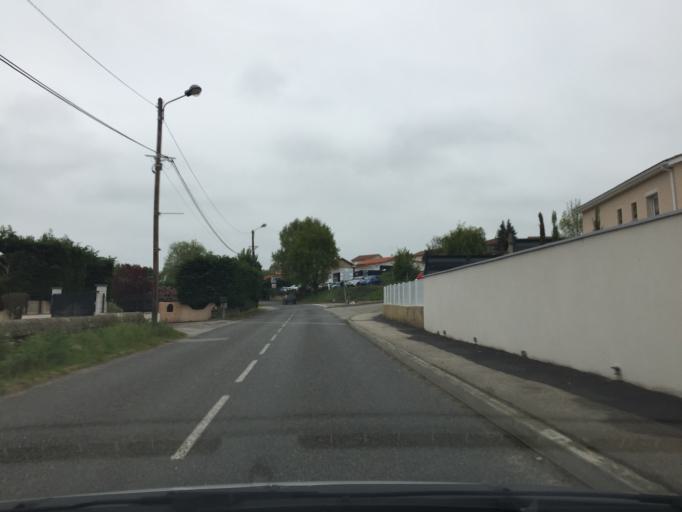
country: FR
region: Rhone-Alpes
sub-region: Departement du Rhone
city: Mornant
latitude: 45.6139
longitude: 4.6706
